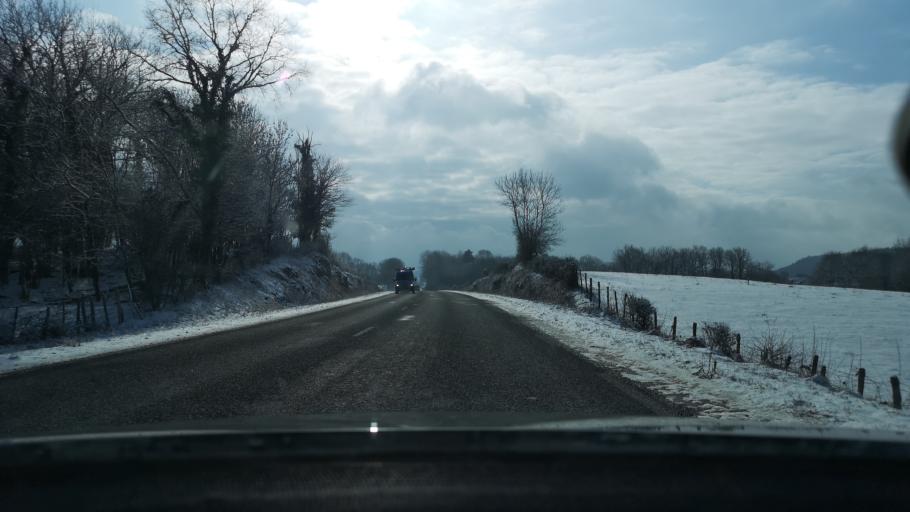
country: FR
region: Franche-Comte
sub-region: Departement du Jura
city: Orgelet
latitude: 46.5662
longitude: 5.5947
